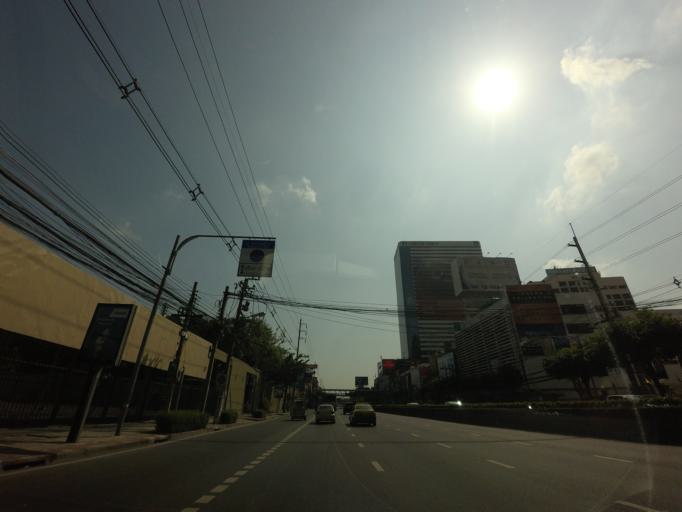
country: TH
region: Bangkok
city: Bang Rak
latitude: 13.7250
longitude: 100.5477
